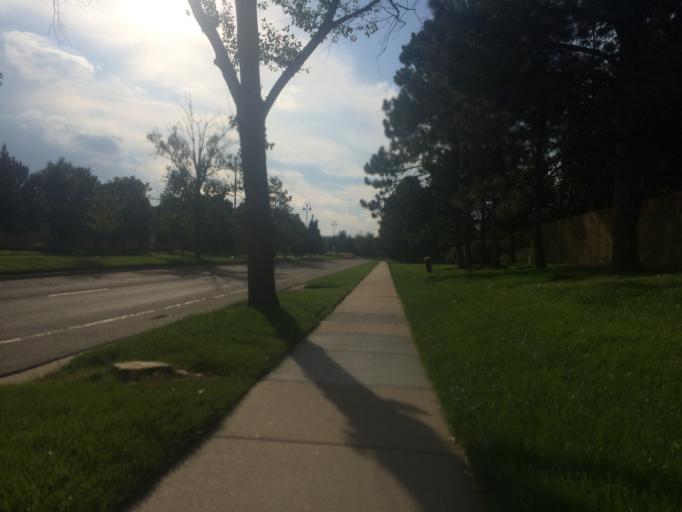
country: US
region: Colorado
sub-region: Boulder County
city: Superior
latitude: 39.9390
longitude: -105.1516
